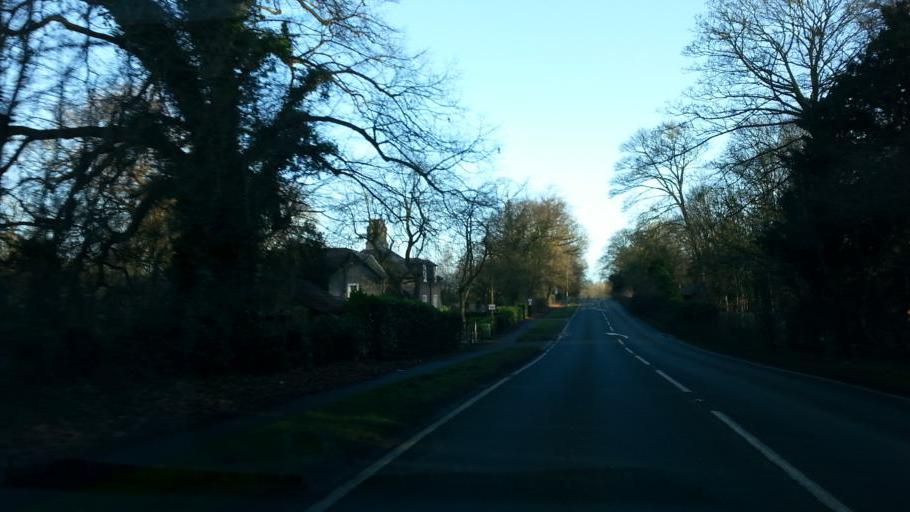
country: GB
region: England
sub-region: Lincolnshire
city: Grantham
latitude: 52.9417
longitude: -0.6244
